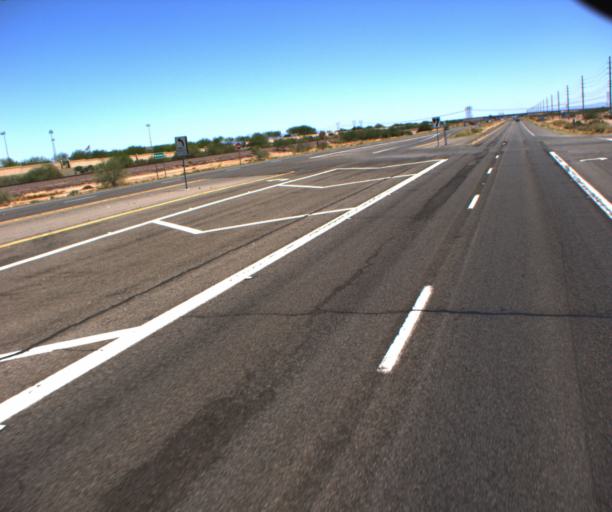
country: US
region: Arizona
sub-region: Maricopa County
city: Sun City West
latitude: 33.6960
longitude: -112.4239
